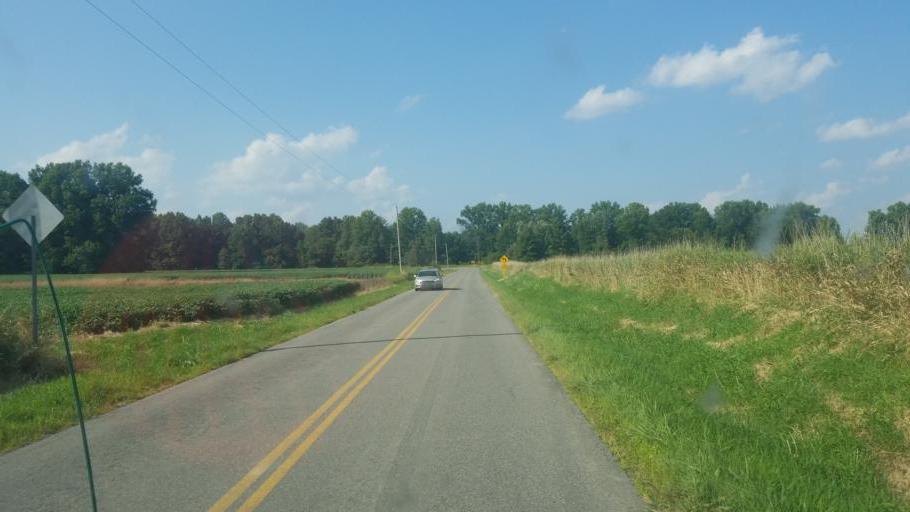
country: US
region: Ohio
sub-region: Medina County
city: Lodi
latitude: 41.0111
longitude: -82.0345
